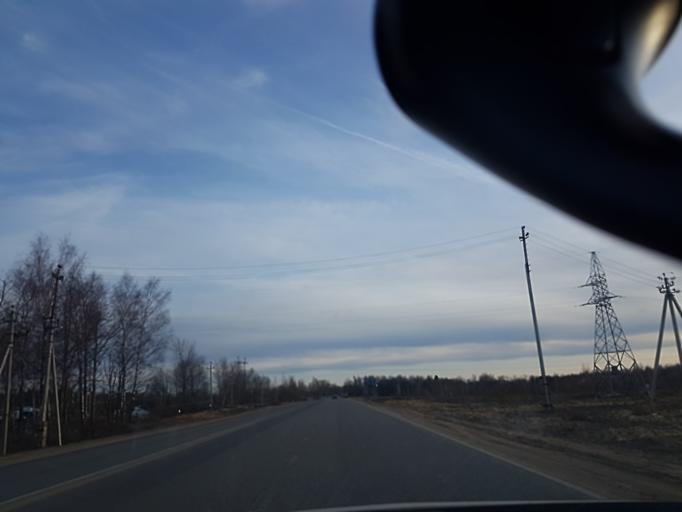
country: RU
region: Moskovskaya
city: Istra
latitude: 55.8797
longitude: 36.8565
